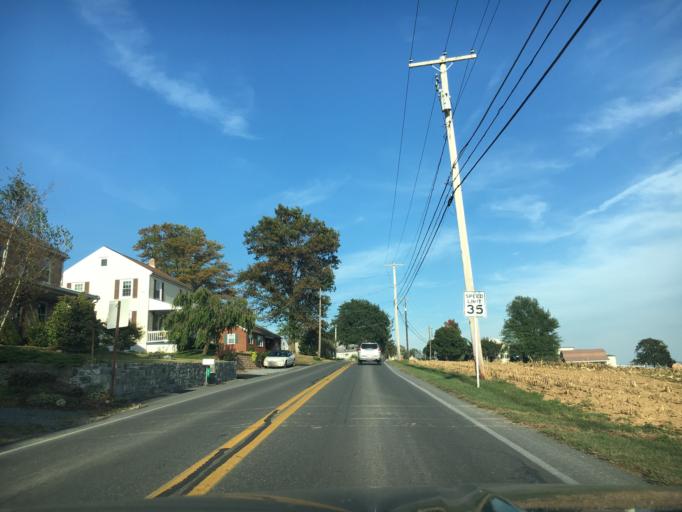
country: US
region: Pennsylvania
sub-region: Lancaster County
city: Akron
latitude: 40.1293
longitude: -76.1584
